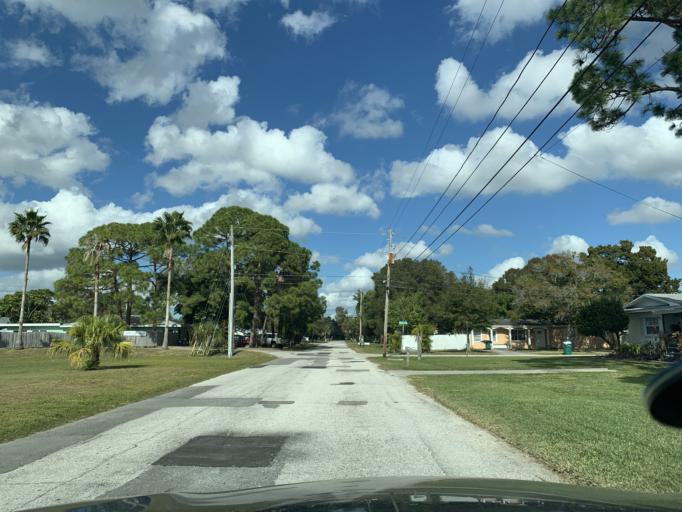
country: US
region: Florida
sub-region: Pinellas County
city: Kenneth City
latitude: 27.8087
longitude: -82.7456
